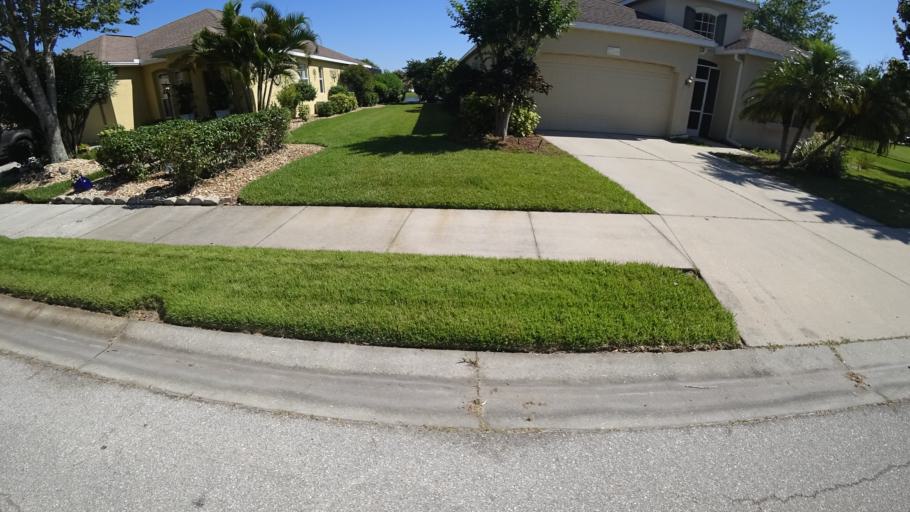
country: US
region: Florida
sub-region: Manatee County
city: Ellenton
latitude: 27.5642
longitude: -82.4392
